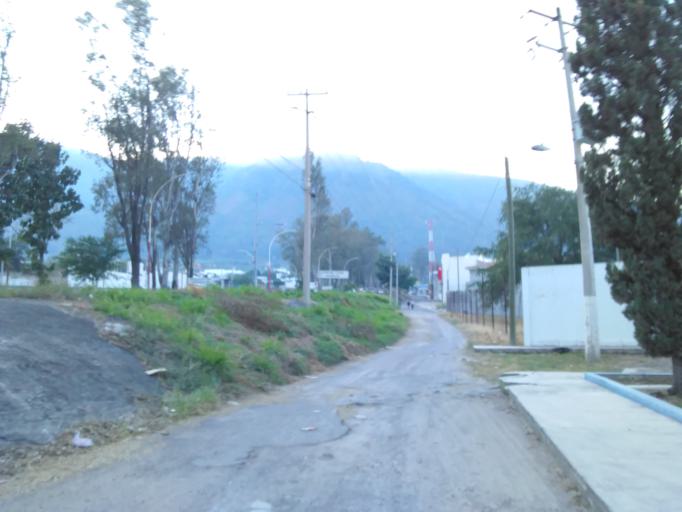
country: MX
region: Nayarit
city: Tepic
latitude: 21.5012
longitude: -104.9142
